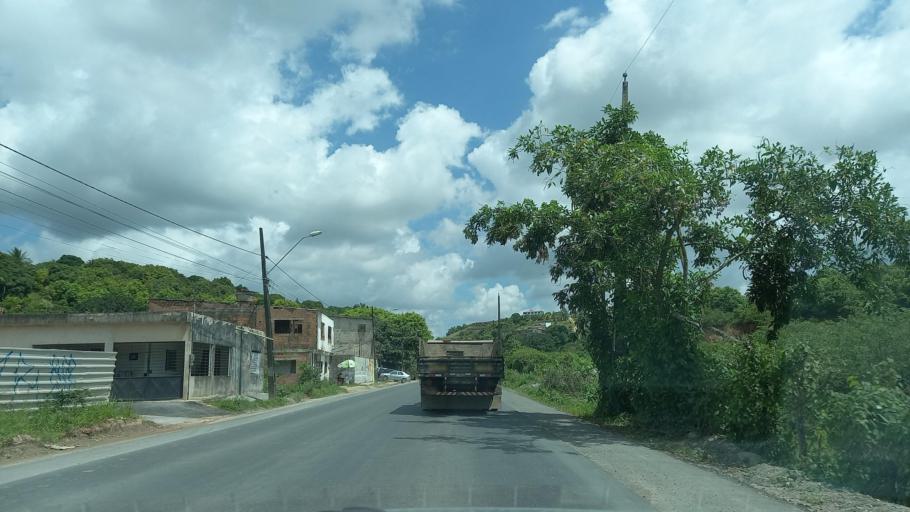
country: BR
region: Pernambuco
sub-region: Jaboatao Dos Guararapes
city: Jaboatao dos Guararapes
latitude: -8.1214
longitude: -35.0058
